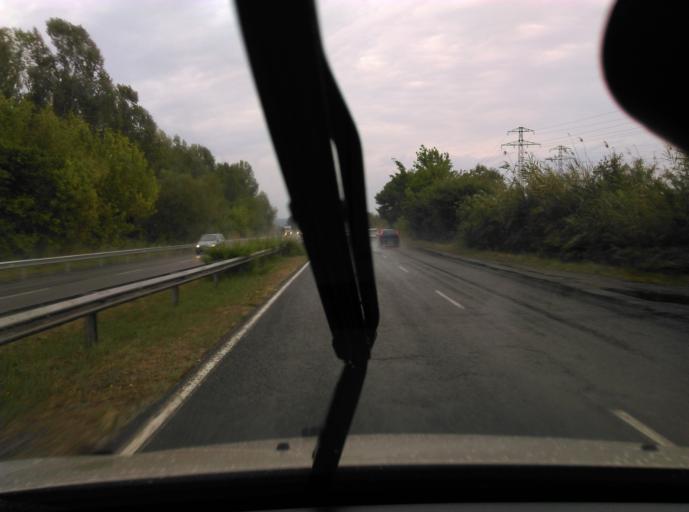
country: BG
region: Burgas
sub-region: Obshtina Burgas
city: Burgas
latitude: 42.4586
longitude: 27.4400
